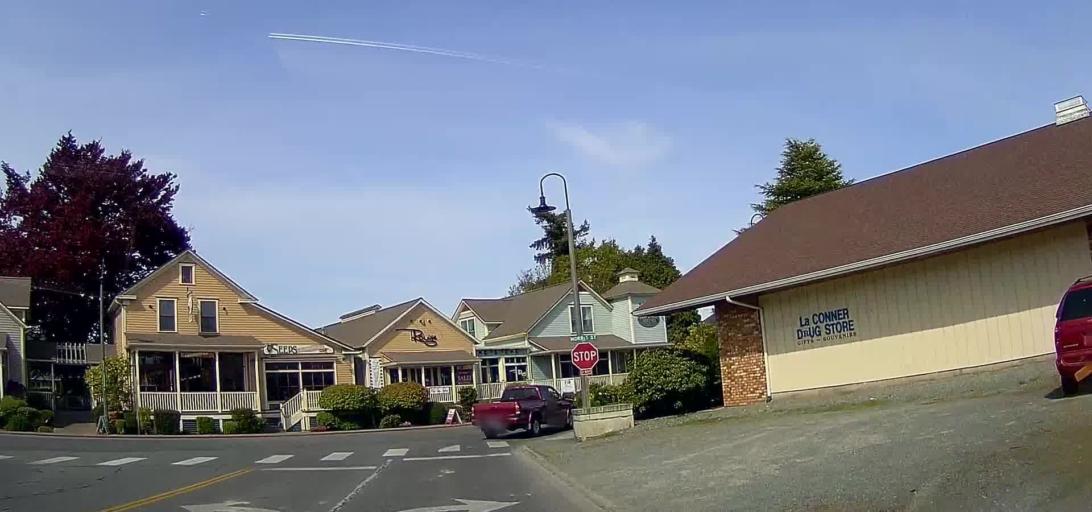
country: US
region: Washington
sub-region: Skagit County
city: Mount Vernon
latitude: 48.3920
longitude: -122.4894
